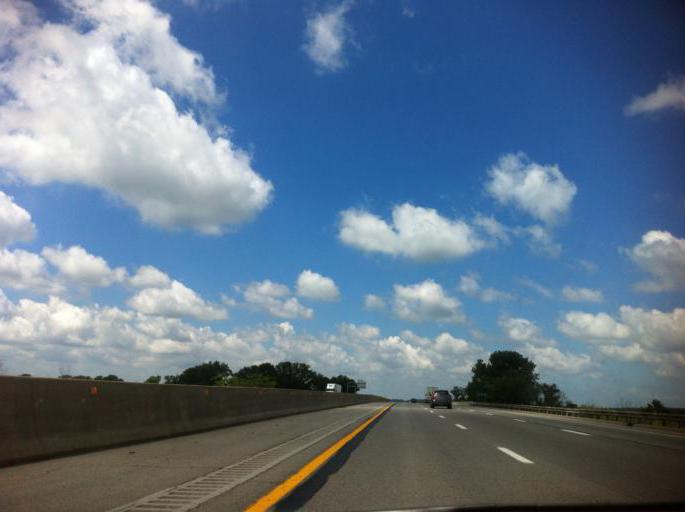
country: US
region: Ohio
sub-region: Erie County
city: Milan
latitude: 41.3252
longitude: -82.6292
